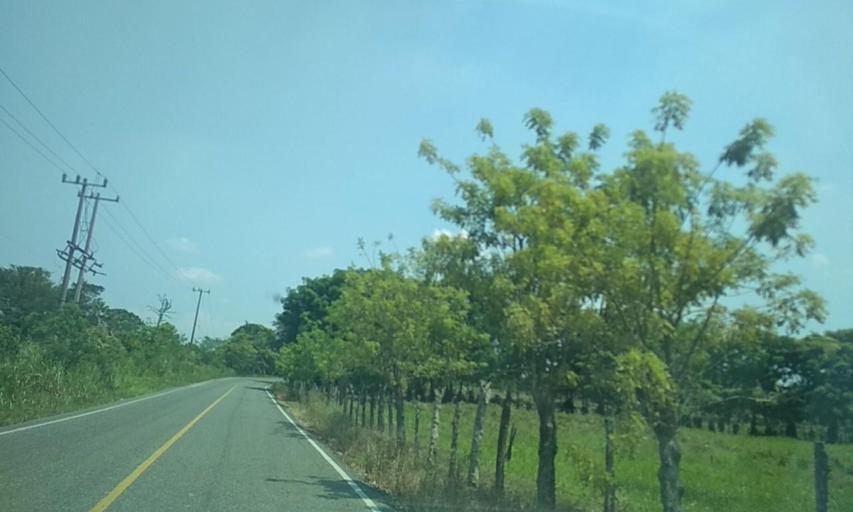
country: MX
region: Tabasco
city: Huimanguillo
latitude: 17.8179
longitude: -93.4974
